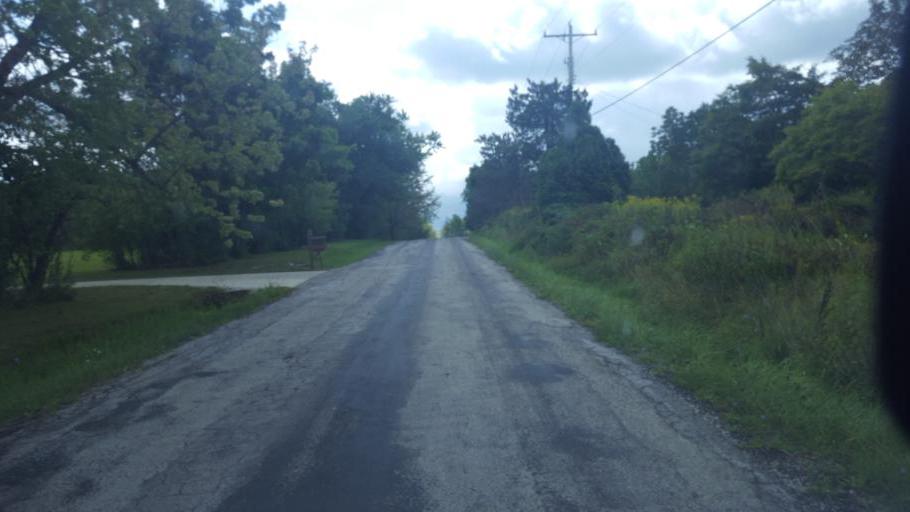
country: US
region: Ohio
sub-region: Geauga County
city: Chardon
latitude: 41.6429
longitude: -81.1126
